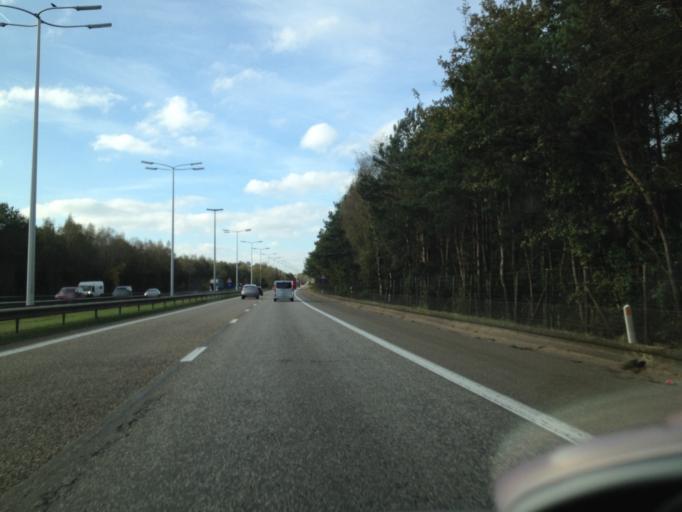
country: BE
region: Flanders
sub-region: Provincie Limburg
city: Maasmechelen
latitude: 50.9561
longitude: 5.6633
